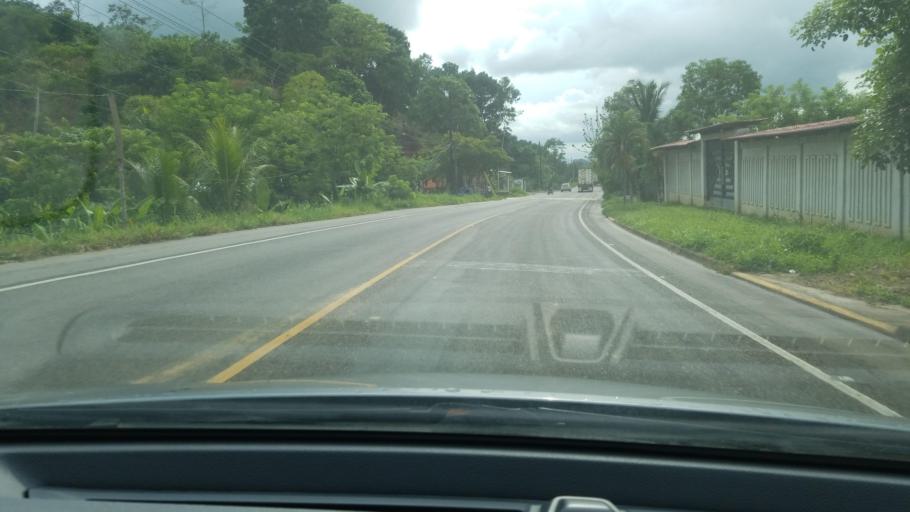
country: HN
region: Cortes
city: Potrerillos
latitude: 15.5938
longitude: -88.3098
